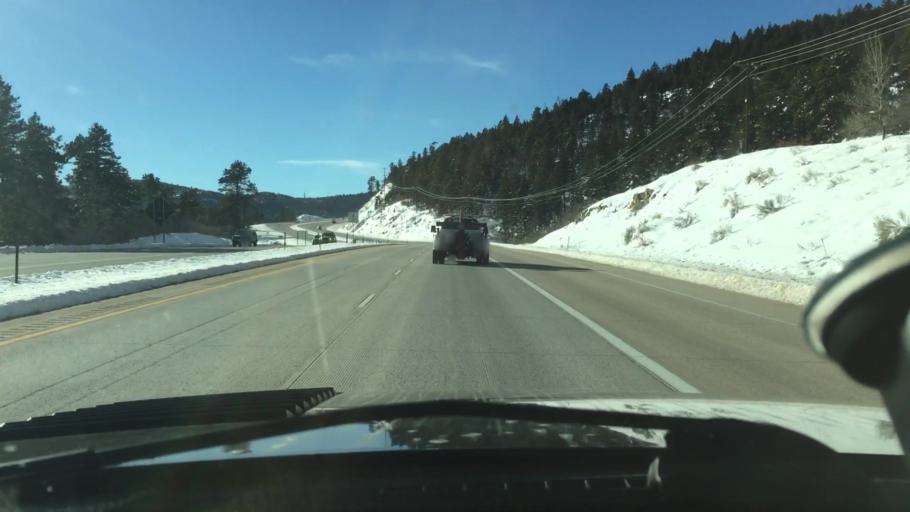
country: US
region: Colorado
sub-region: Jefferson County
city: Indian Hills
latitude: 39.5625
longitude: -105.2395
